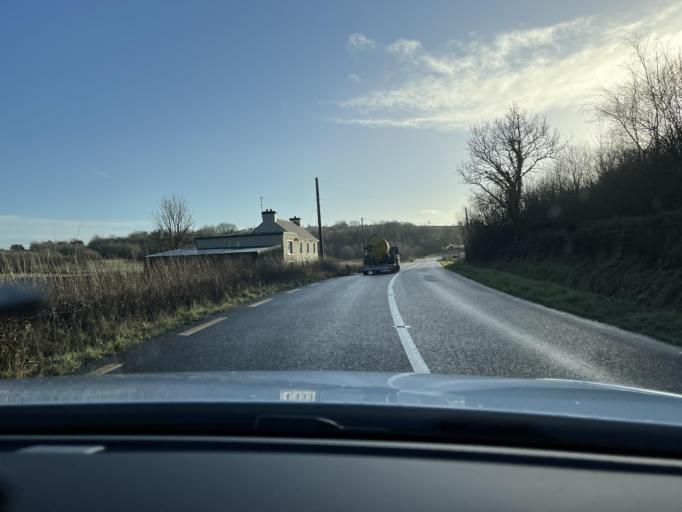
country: IE
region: Connaught
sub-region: County Leitrim
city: Manorhamilton
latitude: 54.2264
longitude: -8.2044
